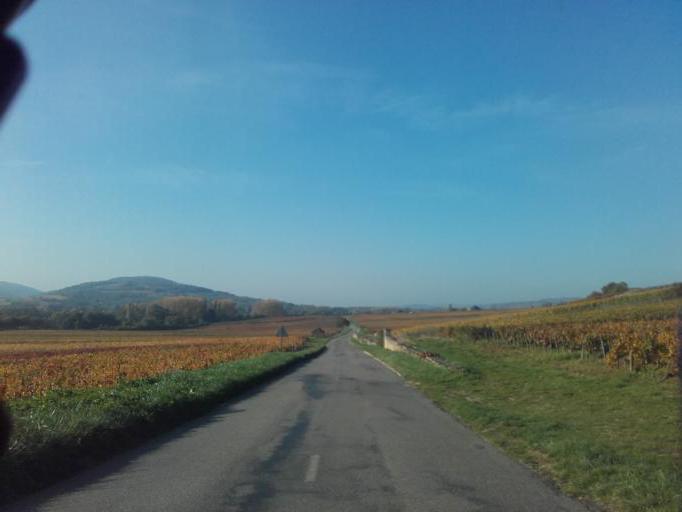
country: FR
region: Bourgogne
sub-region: Departement de Saone-et-Loire
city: Chagny
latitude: 46.9189
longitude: 4.7168
